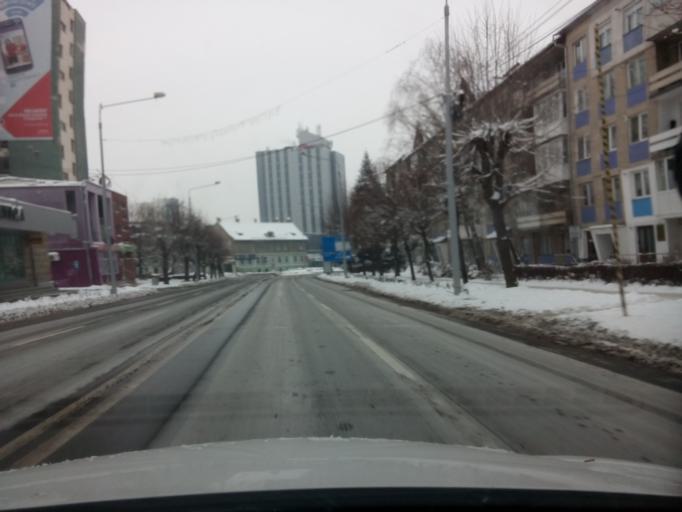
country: RO
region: Sibiu
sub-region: Municipiul Sibiu
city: Sibiu
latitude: 45.7886
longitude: 24.1517
